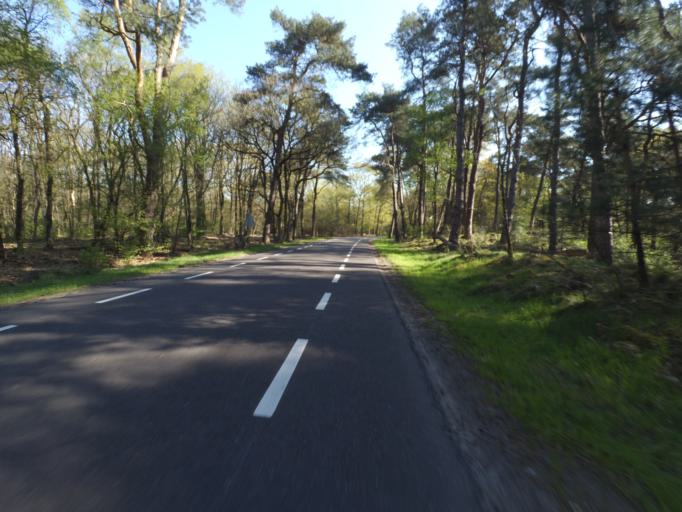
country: NL
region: Gelderland
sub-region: Gemeente Ede
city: Harskamp
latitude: 52.1739
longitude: 5.7457
